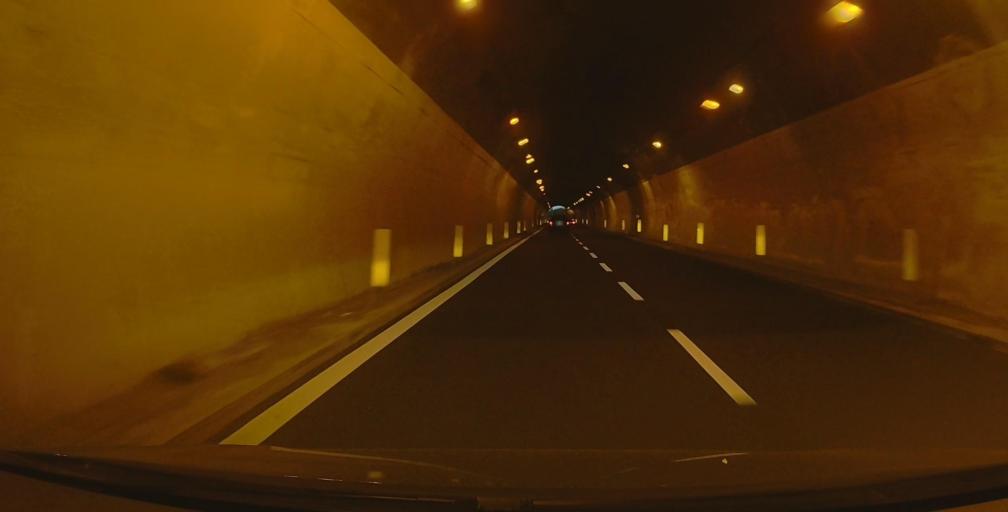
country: IT
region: Sicily
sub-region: Messina
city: Scaletta Zanclea
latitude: 38.0723
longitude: 15.4885
